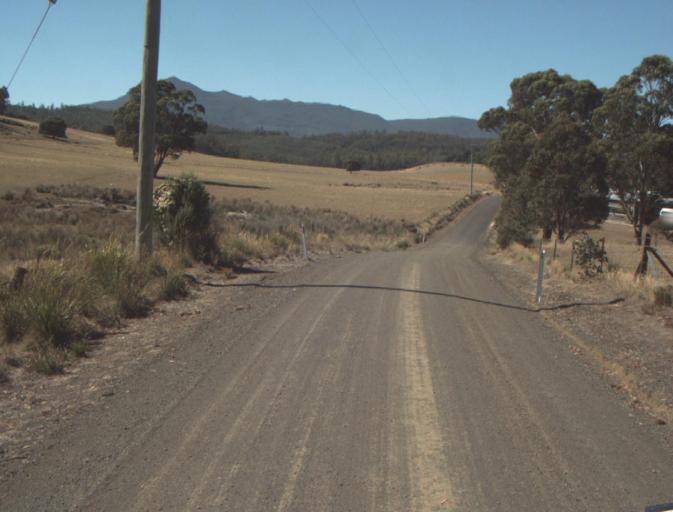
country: AU
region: Tasmania
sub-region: Launceston
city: Newstead
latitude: -41.3055
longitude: 147.3174
